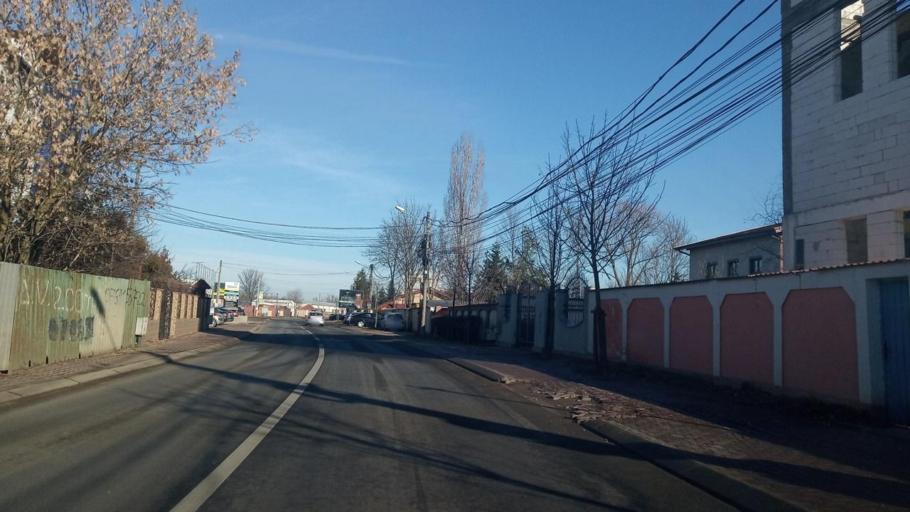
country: RO
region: Ilfov
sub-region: Comuna Chitila
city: Chitila
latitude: 44.5088
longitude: 25.9842
